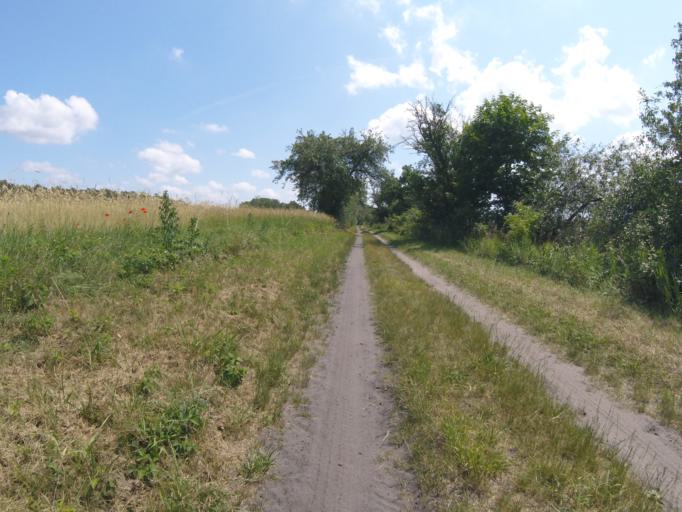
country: DE
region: Brandenburg
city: Bestensee
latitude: 52.2666
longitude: 13.7036
